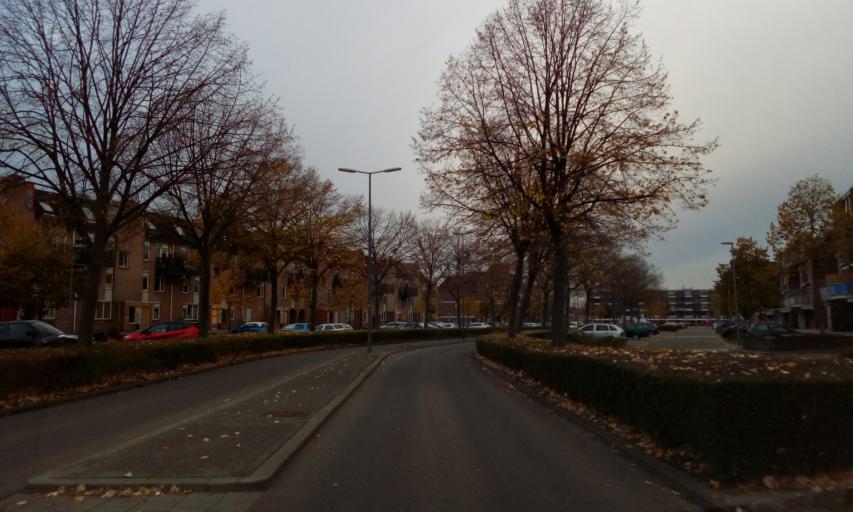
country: NL
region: South Holland
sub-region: Gemeente Capelle aan den IJssel
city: Capelle aan den IJssel
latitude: 51.9631
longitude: 4.5637
